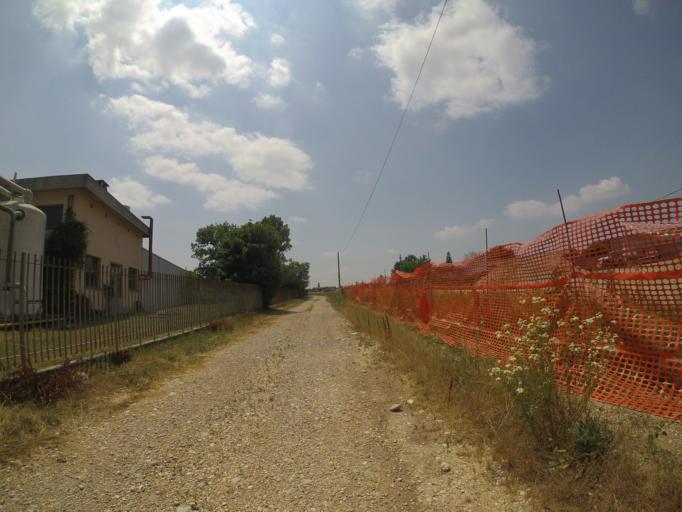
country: IT
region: Friuli Venezia Giulia
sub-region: Provincia di Udine
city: Bertiolo
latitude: 45.9508
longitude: 13.0589
